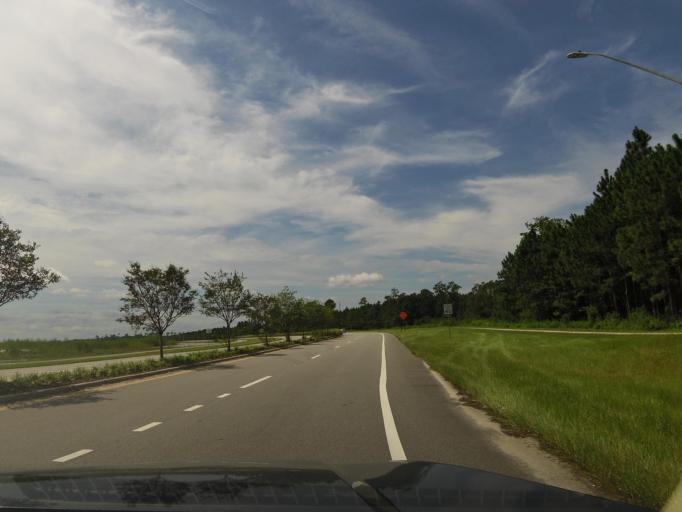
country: US
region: Florida
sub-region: Clay County
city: Green Cove Springs
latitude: 30.0019
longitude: -81.5037
